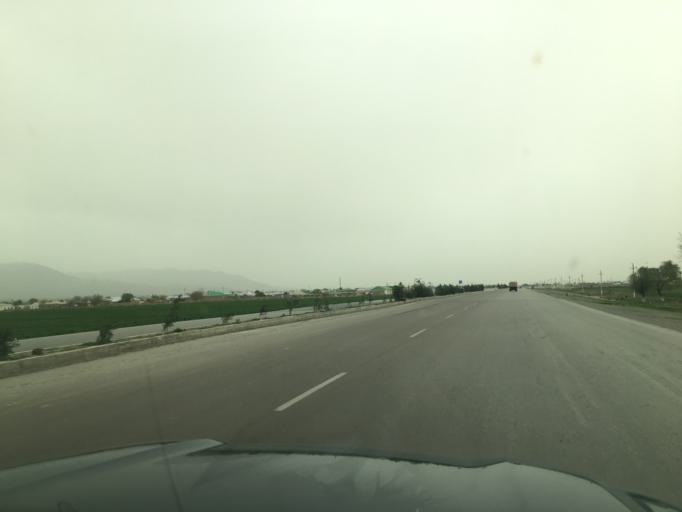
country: TM
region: Ahal
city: Baharly
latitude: 38.3920
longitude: 57.4843
